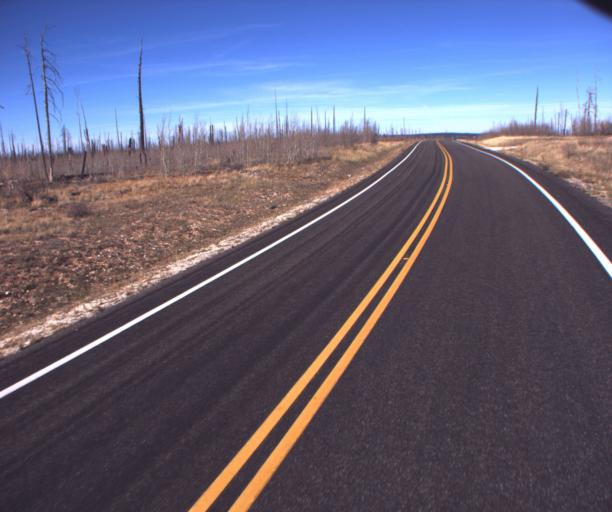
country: US
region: Arizona
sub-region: Coconino County
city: Grand Canyon
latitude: 36.5589
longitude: -112.1712
